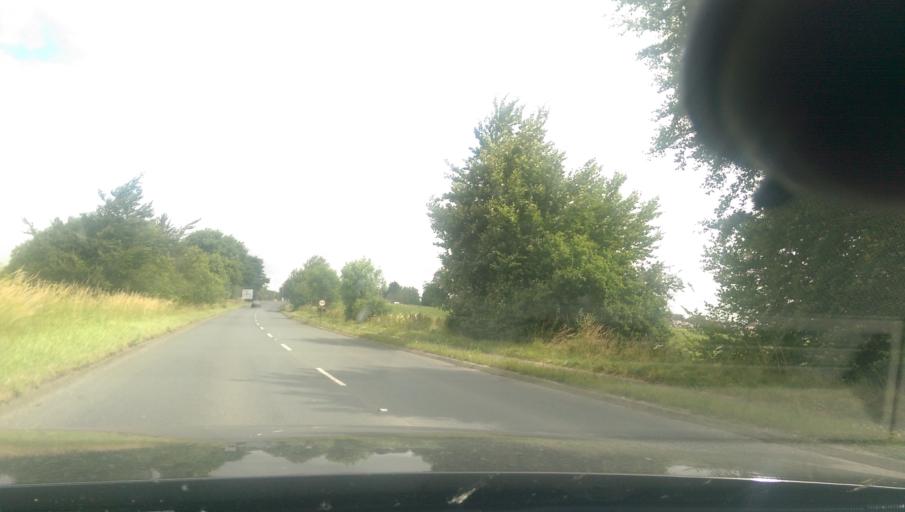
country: GB
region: England
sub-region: Wiltshire
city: Durrington
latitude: 51.1921
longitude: -1.7845
